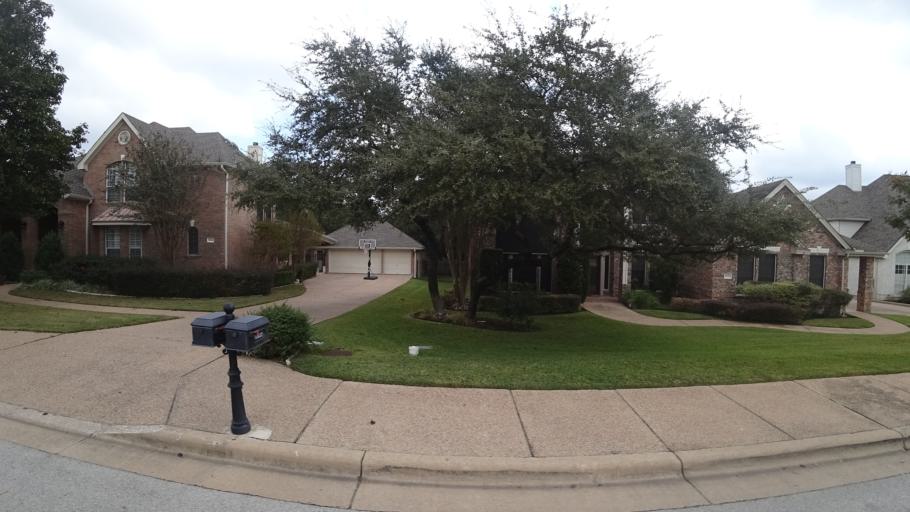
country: US
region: Texas
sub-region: Travis County
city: Barton Creek
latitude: 30.3116
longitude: -97.9005
